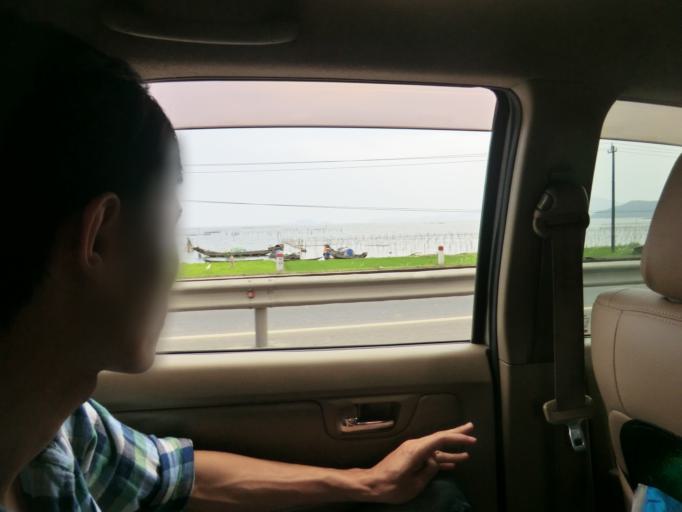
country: VN
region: Thua Thien-Hue
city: Phu Loc
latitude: 16.2911
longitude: 107.8149
